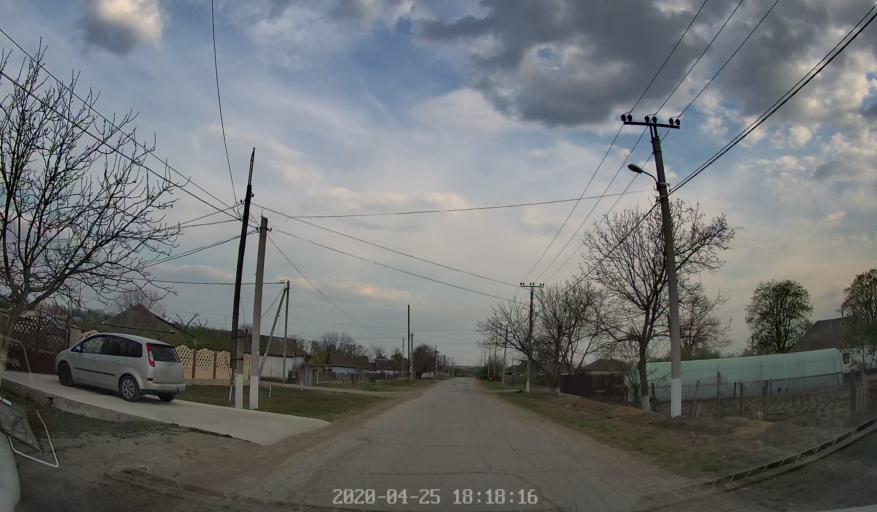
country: MD
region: Criuleni
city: Criuleni
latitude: 47.1651
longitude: 29.1274
